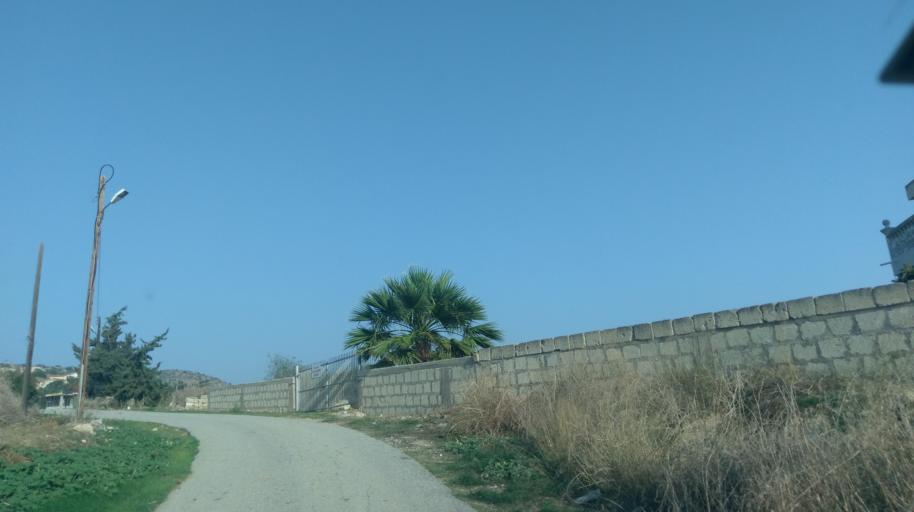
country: CY
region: Ammochostos
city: Leonarisso
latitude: 35.4762
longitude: 34.1035
